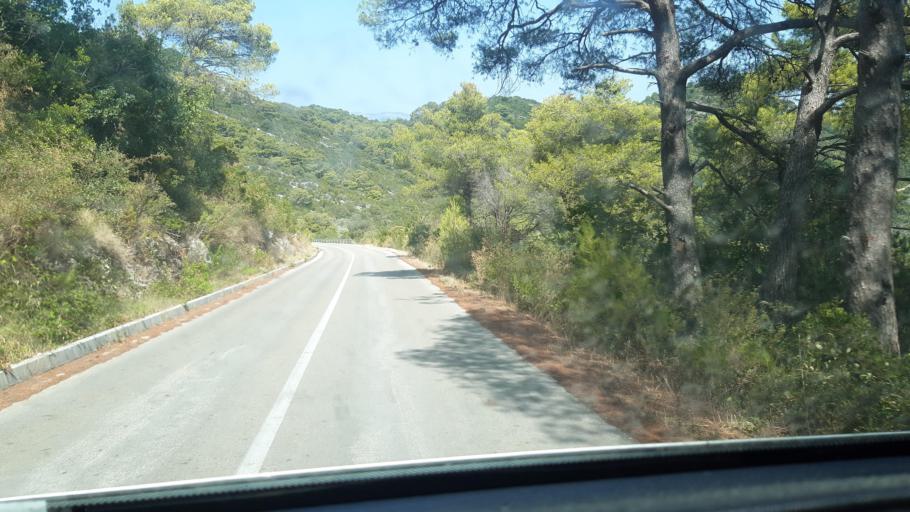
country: HR
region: Dubrovacko-Neretvanska
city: Ston
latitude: 42.7217
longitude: 17.6670
